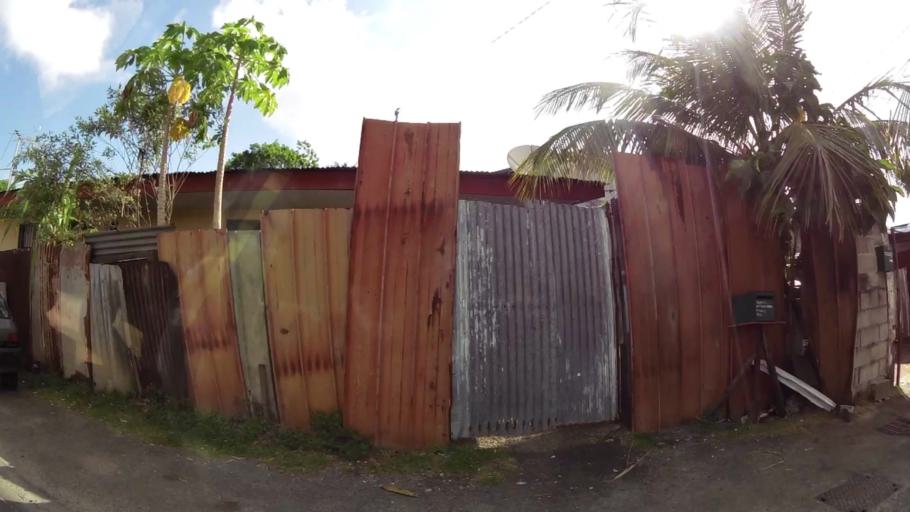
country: GF
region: Guyane
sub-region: Guyane
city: Cayenne
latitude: 4.9327
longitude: -52.3187
